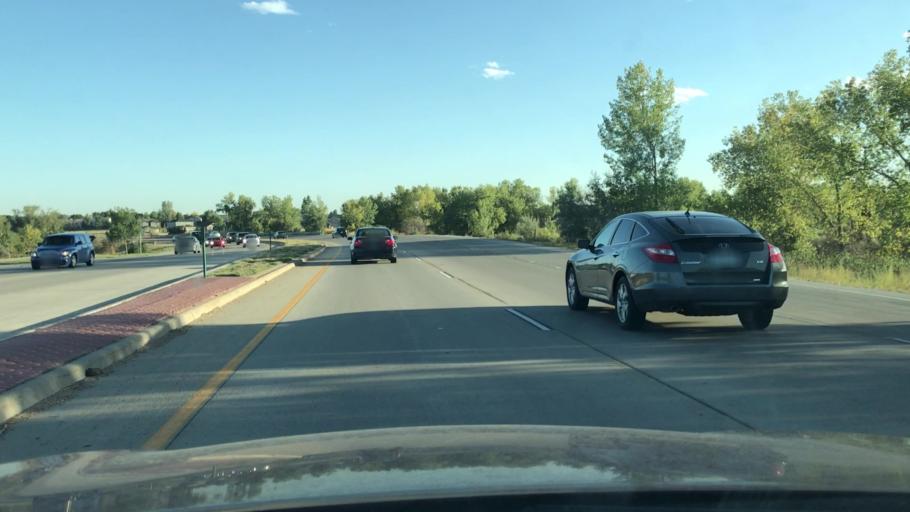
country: US
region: Colorado
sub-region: Boulder County
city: Lafayette
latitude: 39.9821
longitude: -105.0985
